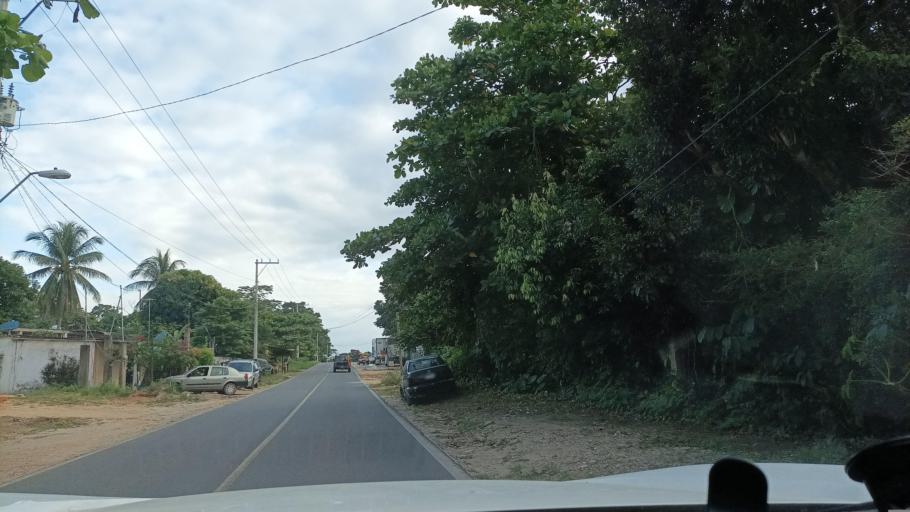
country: MX
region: Veracruz
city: Oluta
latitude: 17.9231
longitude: -94.8885
